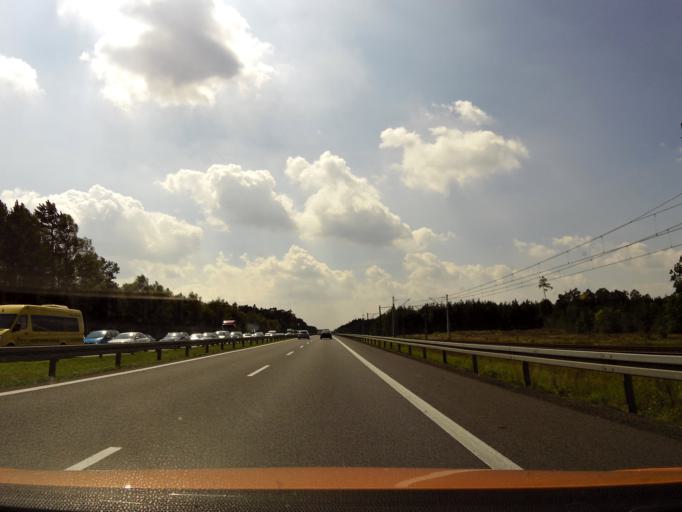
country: PL
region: West Pomeranian Voivodeship
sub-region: Powiat goleniowski
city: Goleniow
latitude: 53.4829
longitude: 14.7922
